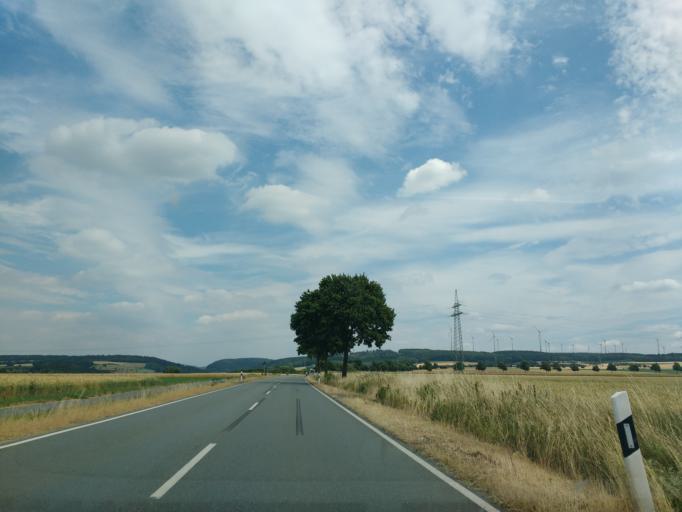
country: DE
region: North Rhine-Westphalia
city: Bad Lippspringe
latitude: 51.7419
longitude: 8.8341
